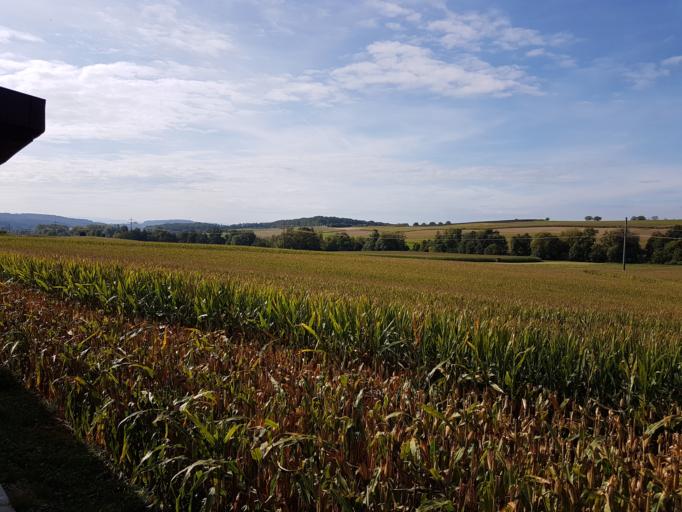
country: DE
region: Baden-Wuerttemberg
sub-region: Freiburg Region
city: Wittlingen
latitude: 47.6827
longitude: 7.6442
